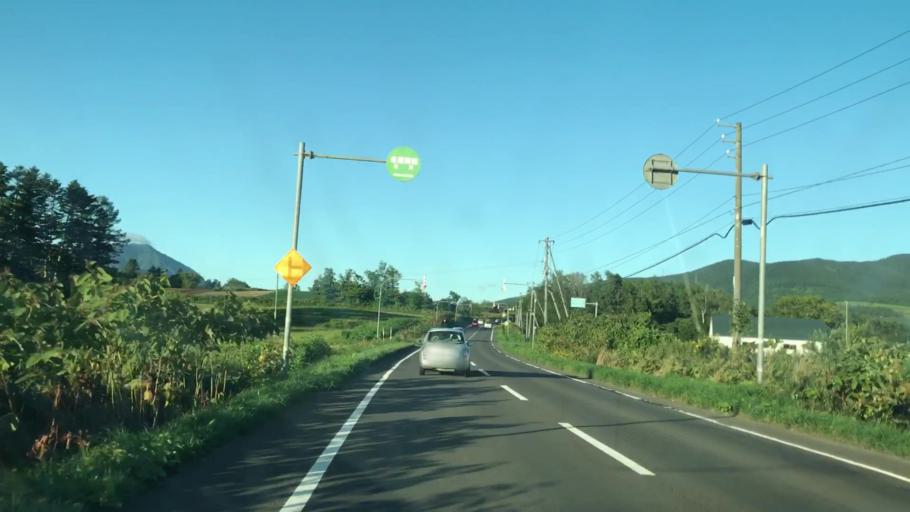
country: JP
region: Hokkaido
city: Niseko Town
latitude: 42.7019
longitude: 140.8489
